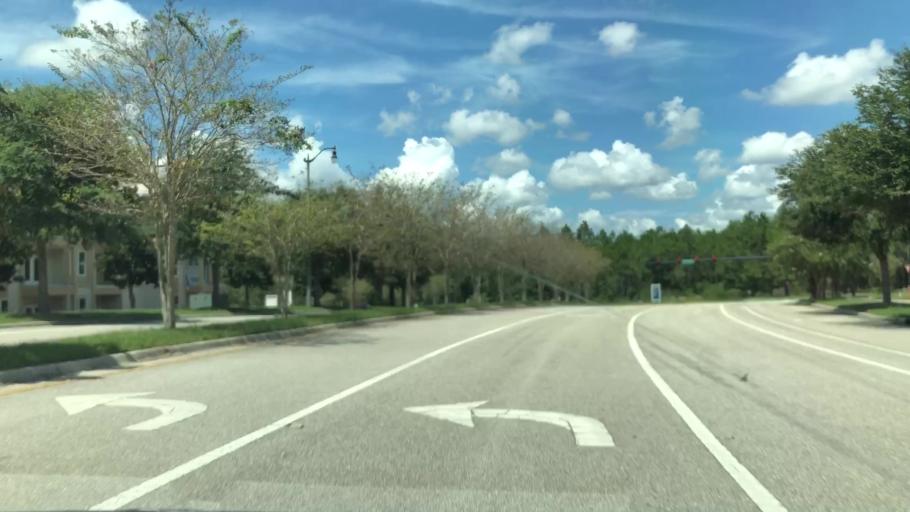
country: US
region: Florida
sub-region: Saint Johns County
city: Palm Valley
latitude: 30.1039
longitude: -81.4423
